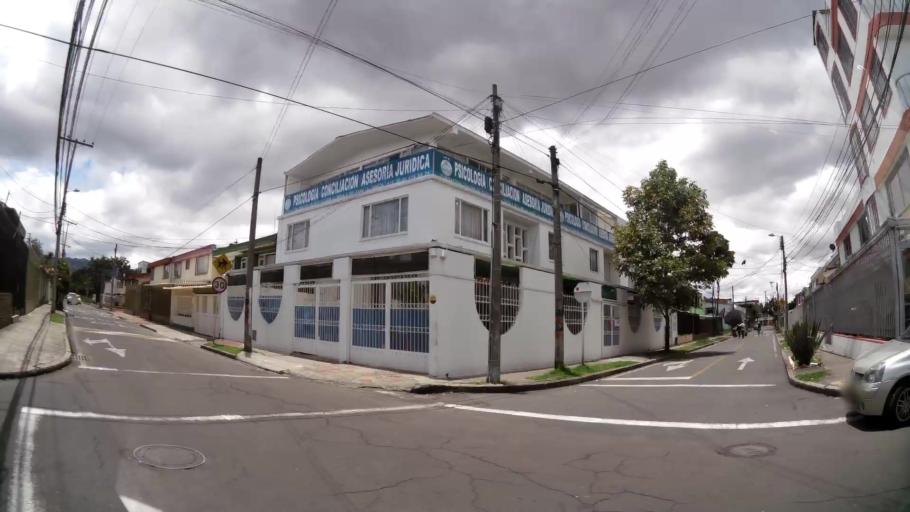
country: CO
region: Bogota D.C.
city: Bogota
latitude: 4.6660
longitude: -74.1081
